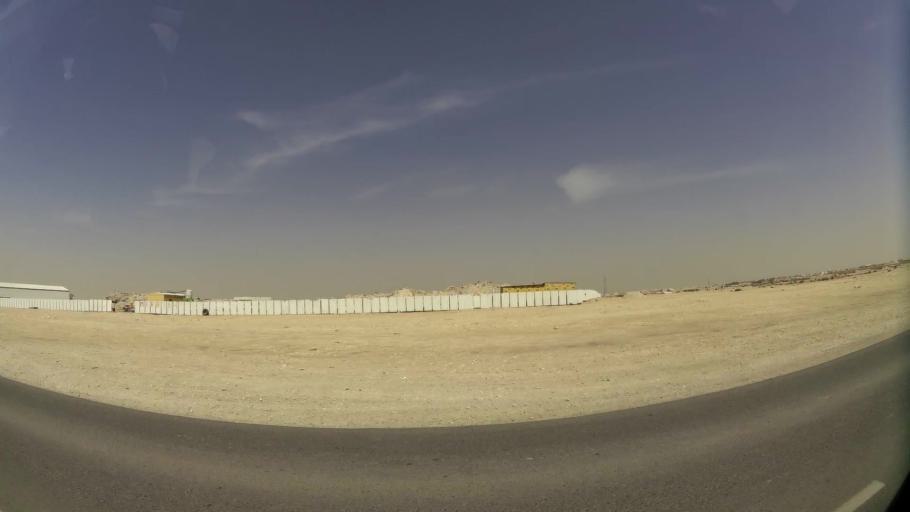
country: QA
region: Baladiyat ar Rayyan
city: Ar Rayyan
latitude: 25.2613
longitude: 51.3815
